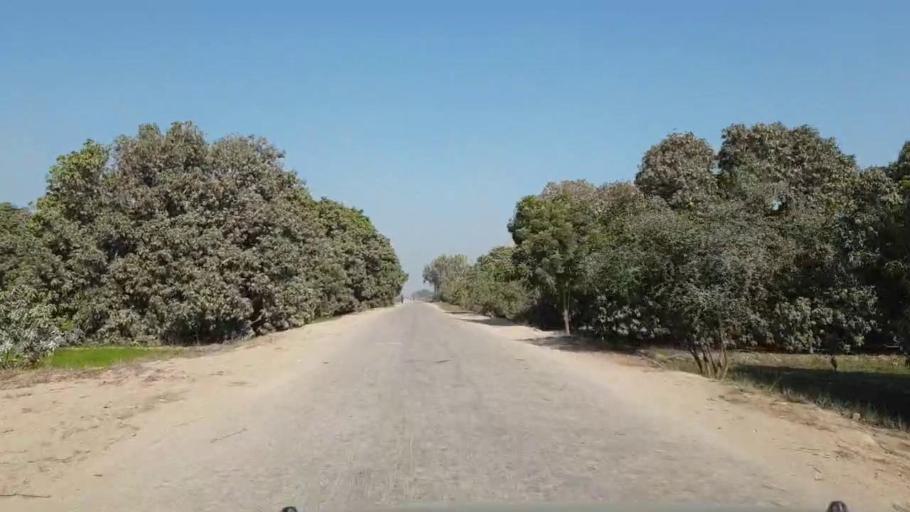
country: PK
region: Sindh
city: Matiari
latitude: 25.5877
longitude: 68.6010
